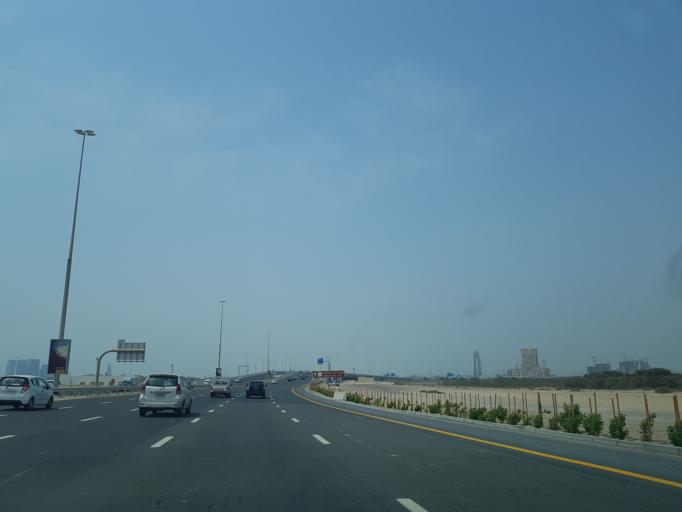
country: AE
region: Ash Shariqah
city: Sharjah
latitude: 25.1947
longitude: 55.3097
